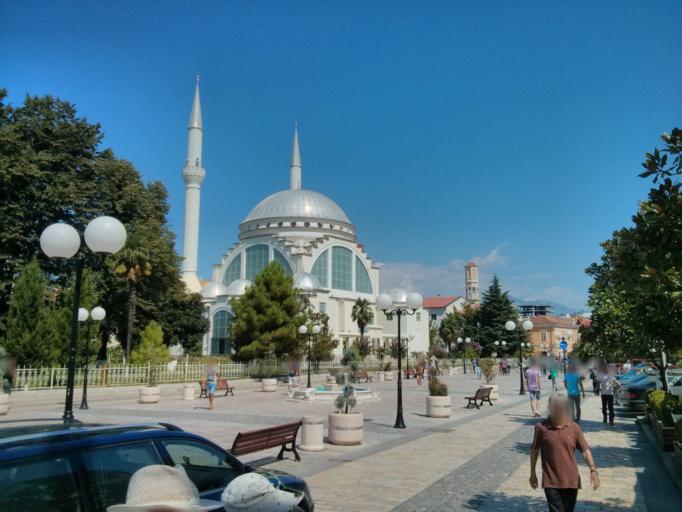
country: AL
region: Shkoder
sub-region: Rrethi i Shkodres
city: Shkoder
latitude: 42.0667
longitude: 19.5139
